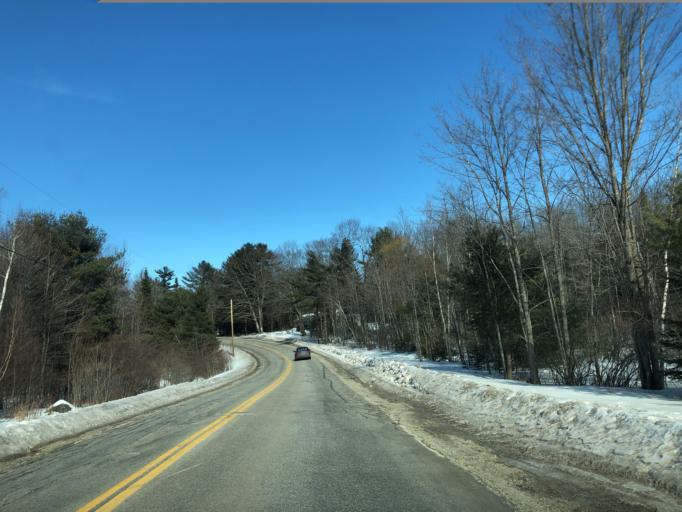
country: US
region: Maine
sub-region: Oxford County
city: Hebron
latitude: 44.2139
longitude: -70.3418
